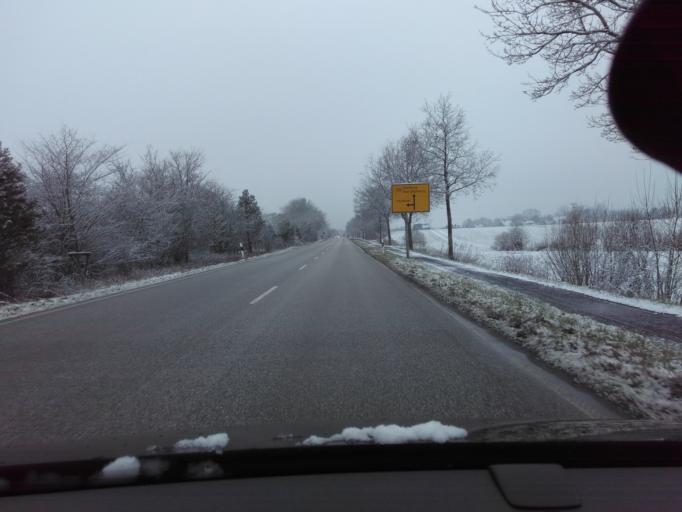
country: DE
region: Schleswig-Holstein
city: Ahrensbok
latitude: 54.0341
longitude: 10.6123
